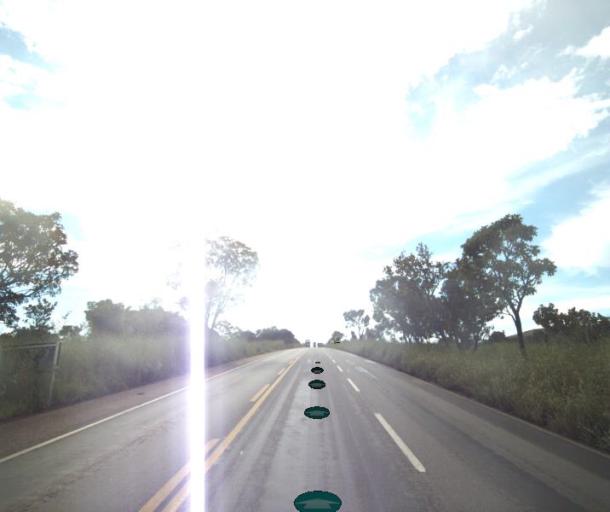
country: BR
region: Goias
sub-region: Jaragua
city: Jaragua
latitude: -15.6277
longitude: -49.3840
